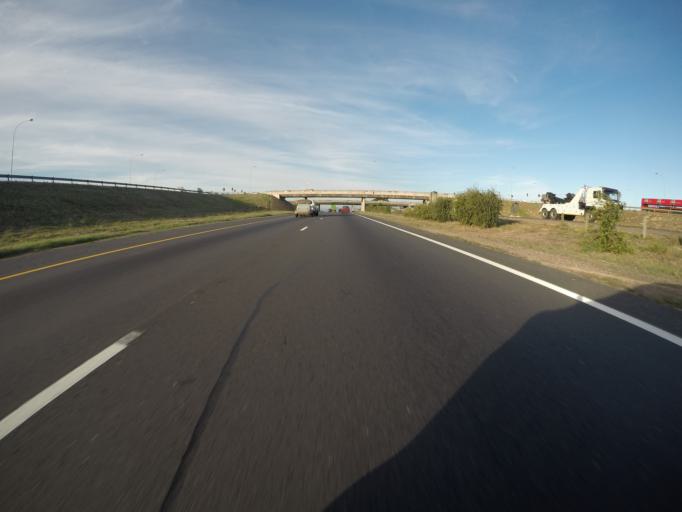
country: ZA
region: Western Cape
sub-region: City of Cape Town
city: Kraaifontein
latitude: -33.8588
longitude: 18.6941
